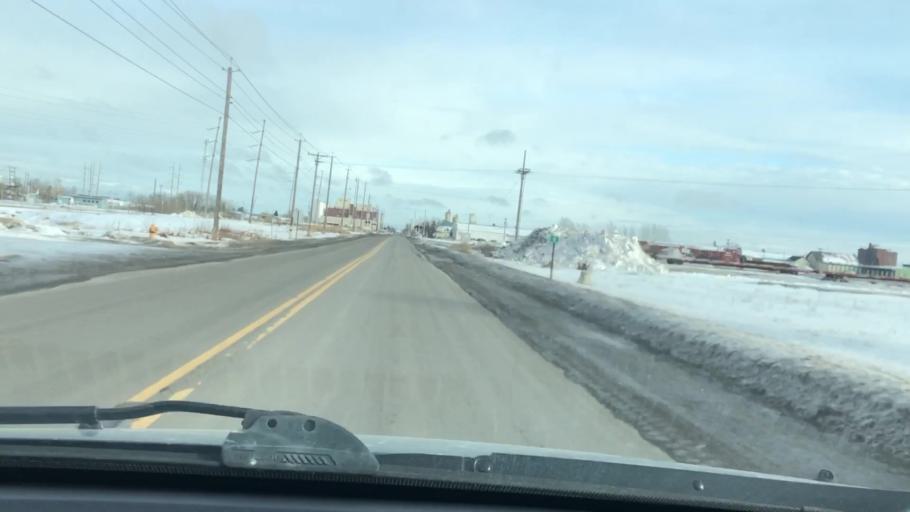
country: US
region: Wisconsin
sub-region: Douglas County
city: Superior
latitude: 46.7279
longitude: -92.1144
